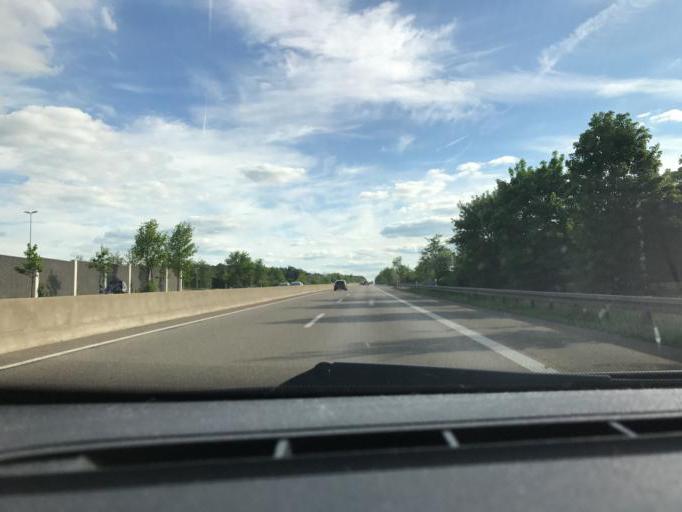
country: DE
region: North Rhine-Westphalia
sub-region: Regierungsbezirk Koln
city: Mechernich
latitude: 50.6077
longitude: 6.7102
